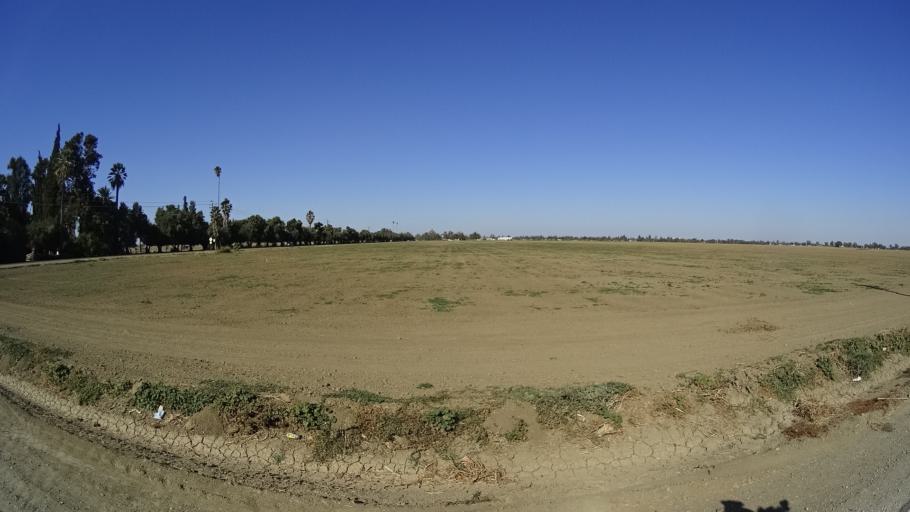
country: US
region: California
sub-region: Yolo County
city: Woodland
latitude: 38.6410
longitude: -121.7839
